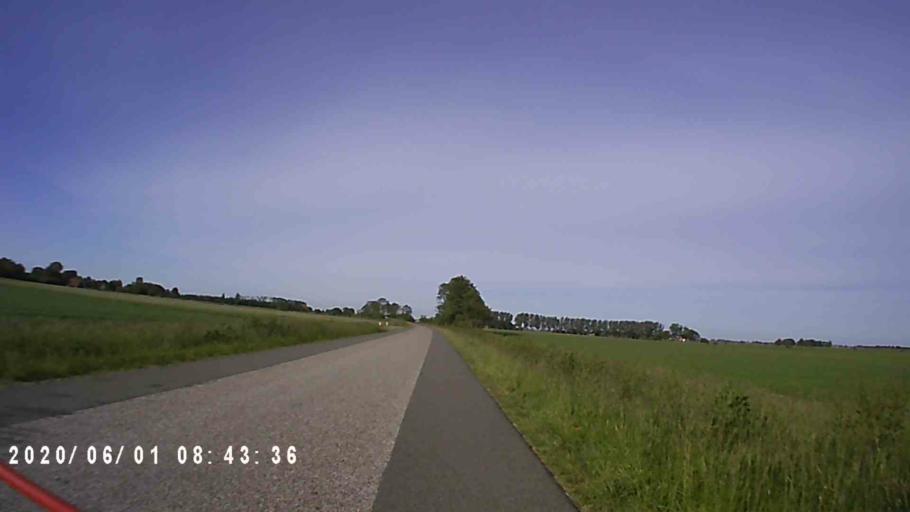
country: NL
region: Friesland
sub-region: Gemeente Ferwerderadiel
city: Burdaard
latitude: 53.2828
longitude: 5.8415
